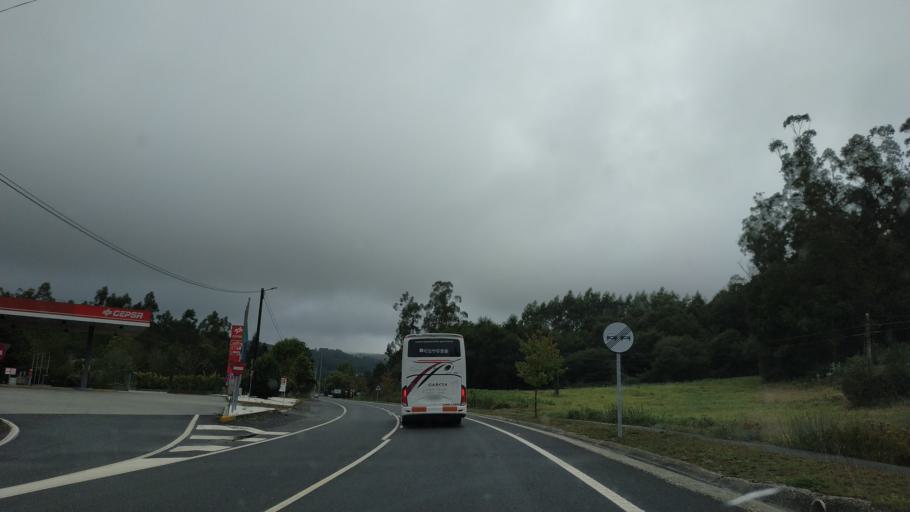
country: ES
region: Galicia
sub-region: Provincia da Coruna
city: Negreira
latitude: 42.9570
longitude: -8.7505
